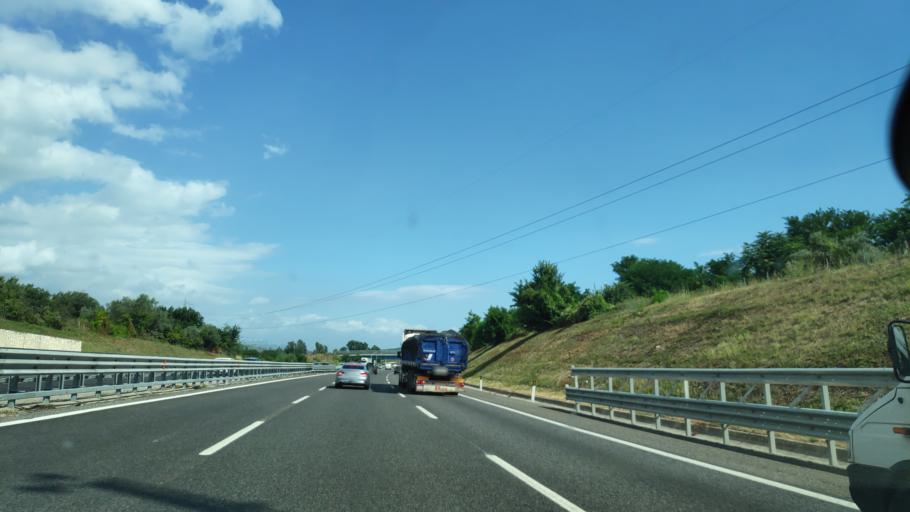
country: IT
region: Campania
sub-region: Provincia di Salerno
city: San Mango Piemonte
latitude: 40.6961
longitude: 14.8295
